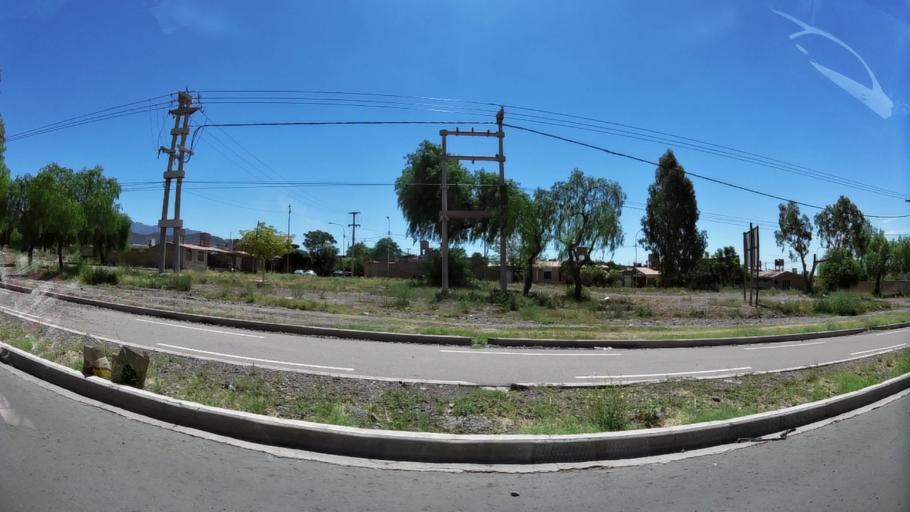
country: AR
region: Mendoza
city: Las Heras
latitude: -32.8533
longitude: -68.8643
